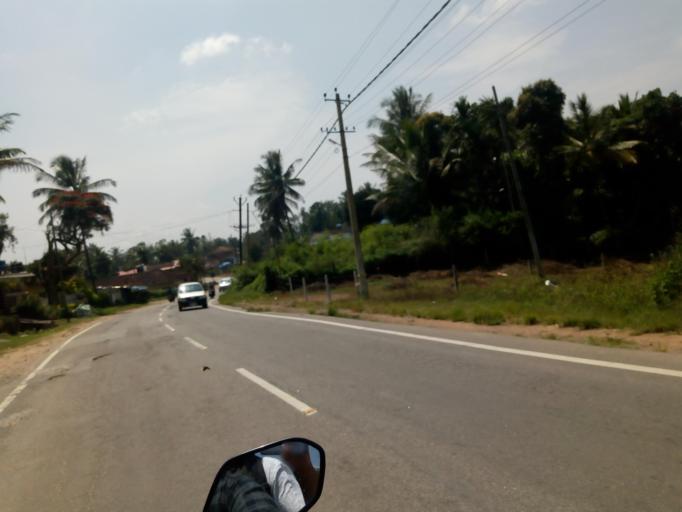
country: IN
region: Karnataka
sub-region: Kodagu
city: Ponnampet
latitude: 12.1568
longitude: 75.9396
